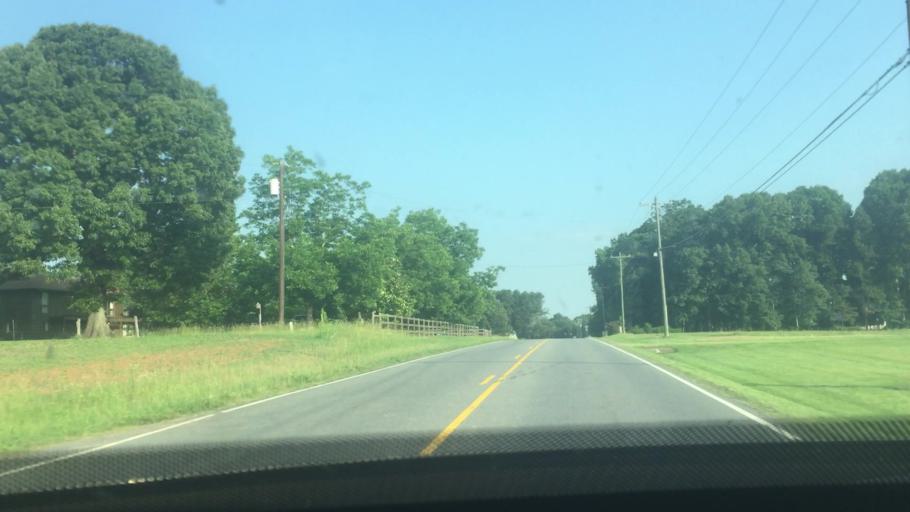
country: US
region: North Carolina
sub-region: Iredell County
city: Mooresville
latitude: 35.5949
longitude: -80.7605
